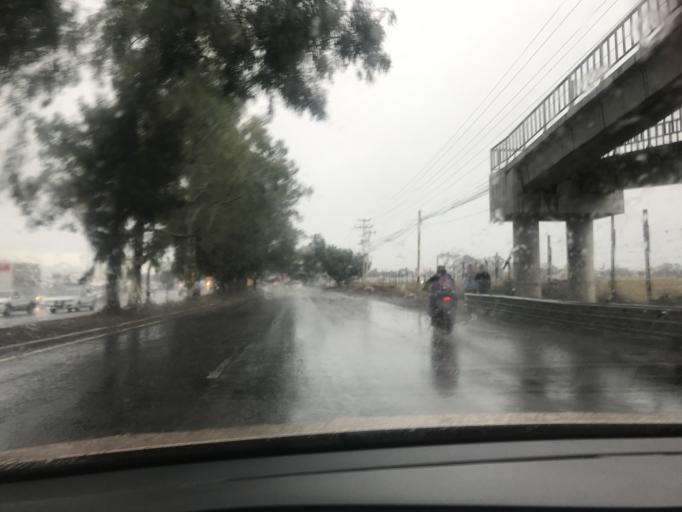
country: MX
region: Mexico
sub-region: Texcoco
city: Santa Martha
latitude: 19.4260
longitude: -98.9107
